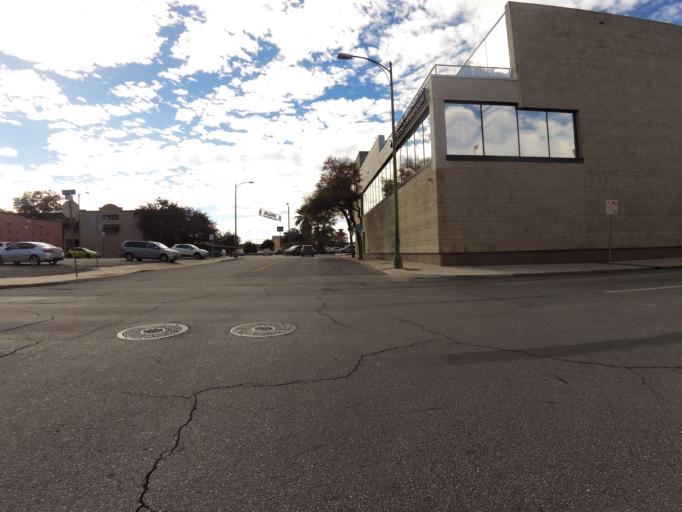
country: US
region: Texas
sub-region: Bexar County
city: San Antonio
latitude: 29.4311
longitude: -98.4934
